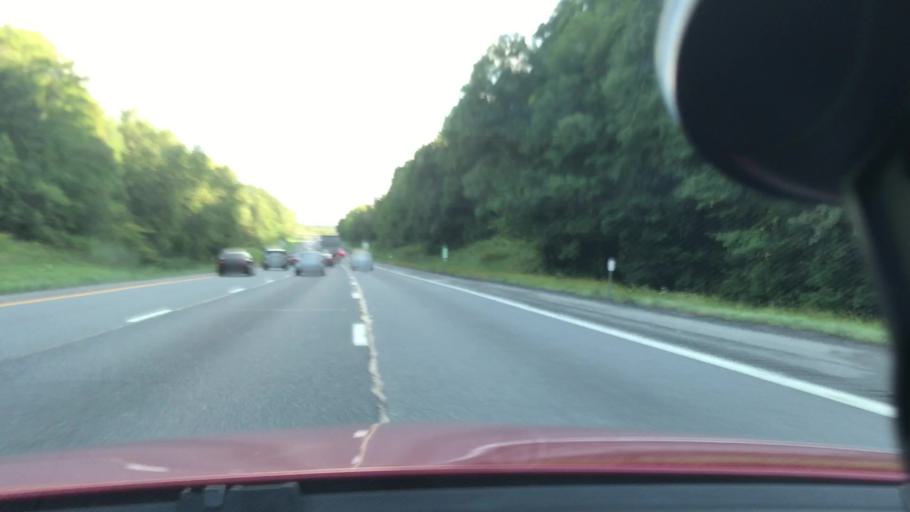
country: US
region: New York
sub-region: Albany County
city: Cohoes
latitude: 42.8096
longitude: -73.7670
